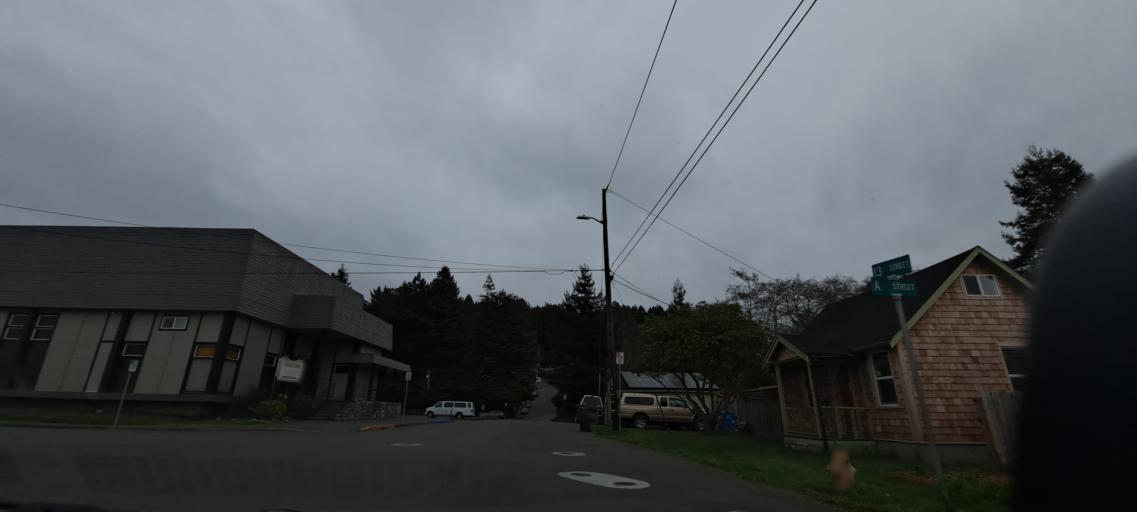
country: US
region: California
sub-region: Humboldt County
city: Arcata
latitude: 40.8707
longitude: -124.0785
